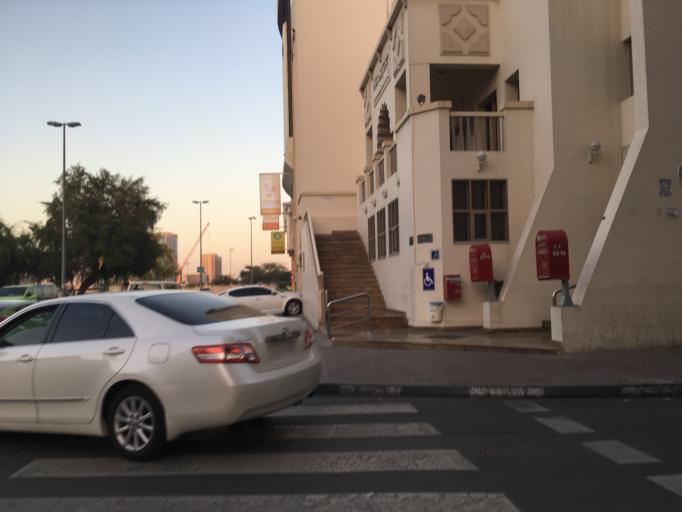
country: AE
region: Ash Shariqah
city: Sharjah
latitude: 25.2630
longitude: 55.2993
